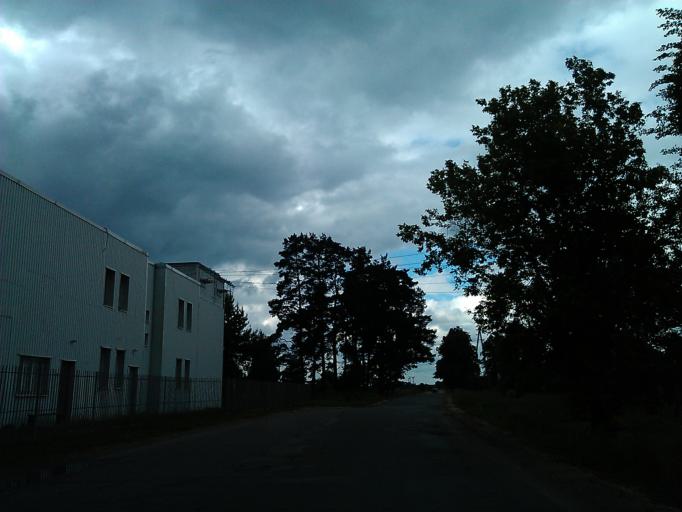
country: LV
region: Adazi
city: Adazi
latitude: 57.0867
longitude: 24.2990
